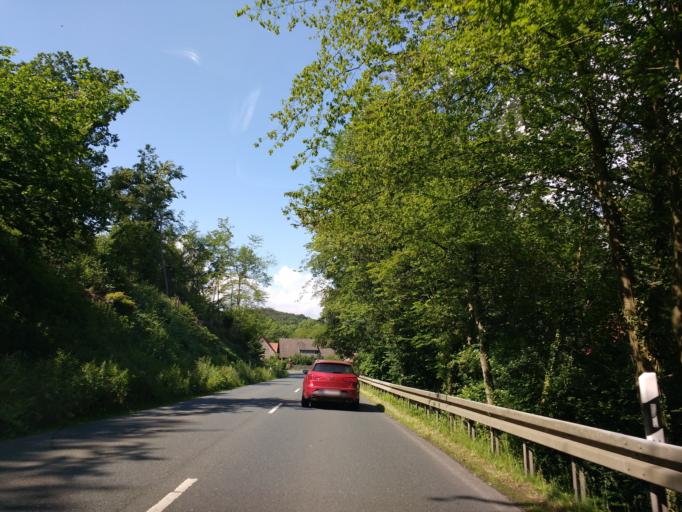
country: DE
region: North Rhine-Westphalia
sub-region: Regierungsbezirk Detmold
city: Vlotho
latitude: 52.1279
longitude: 8.9436
